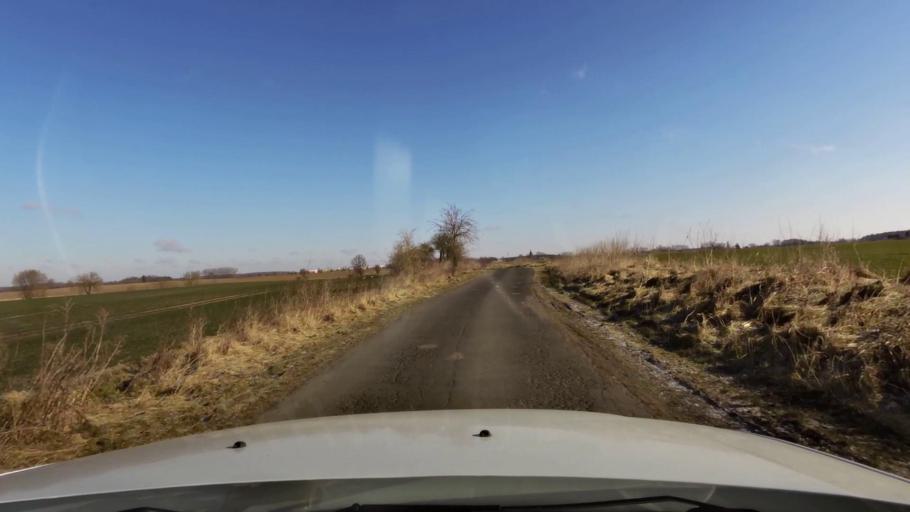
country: PL
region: West Pomeranian Voivodeship
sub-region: Powiat pyrzycki
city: Lipiany
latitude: 52.9842
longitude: 15.0388
